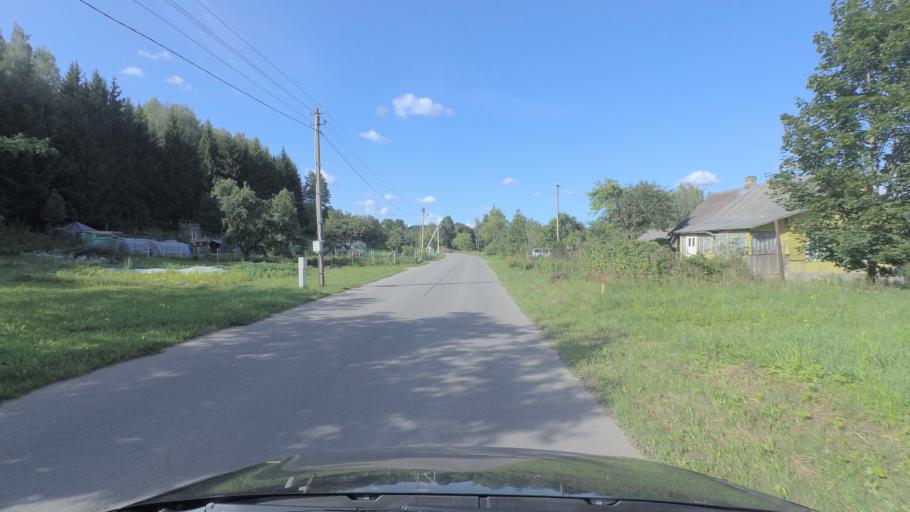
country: LT
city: Nemencine
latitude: 54.8462
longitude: 25.3732
